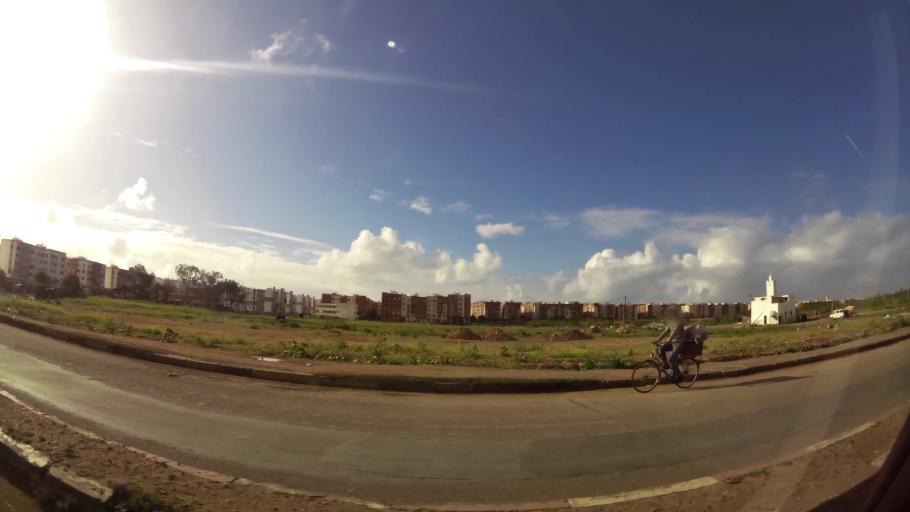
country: MA
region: Grand Casablanca
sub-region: Casablanca
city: Casablanca
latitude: 33.5500
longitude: -7.6979
